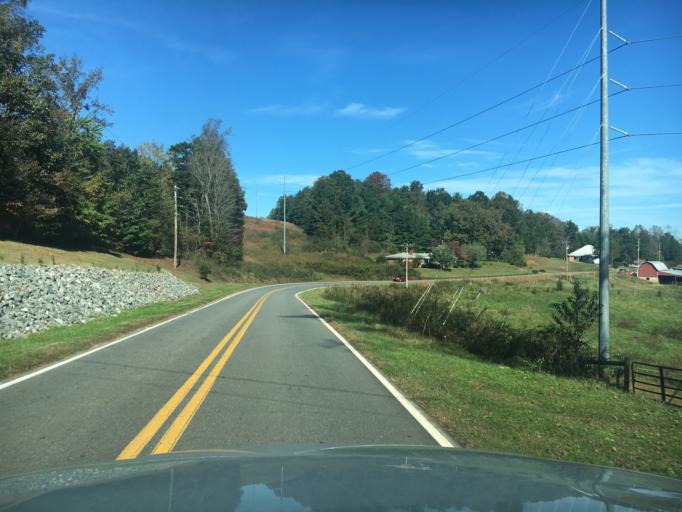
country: US
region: North Carolina
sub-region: Burke County
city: Salem
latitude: 35.7140
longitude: -81.7365
